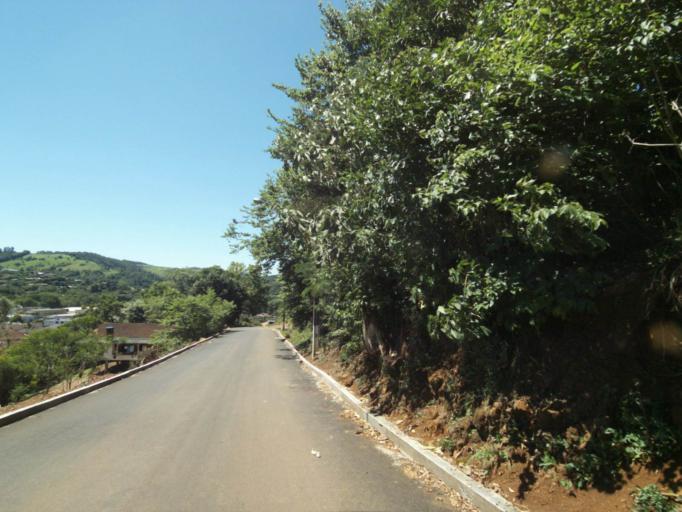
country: BR
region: Parana
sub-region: Ampere
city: Ampere
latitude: -26.1758
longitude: -53.3600
